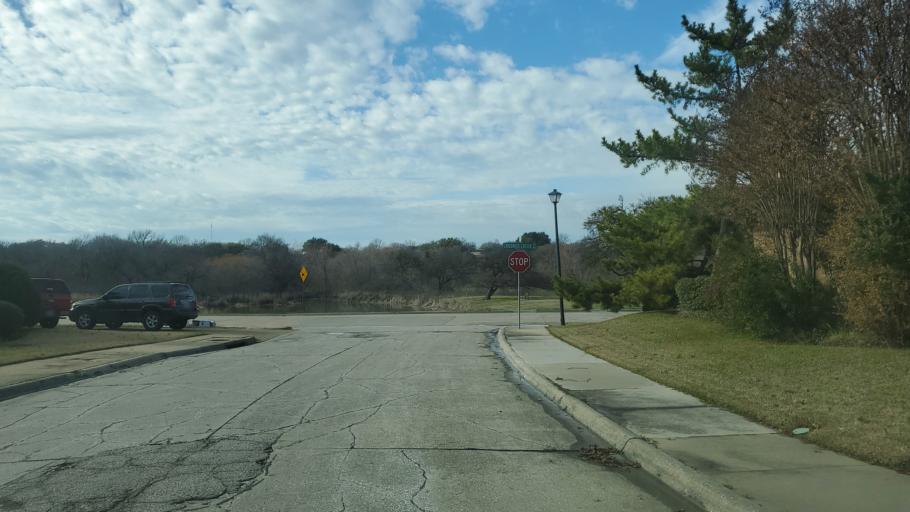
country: US
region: Texas
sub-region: Dallas County
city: Carrollton
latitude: 32.9946
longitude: -96.8935
